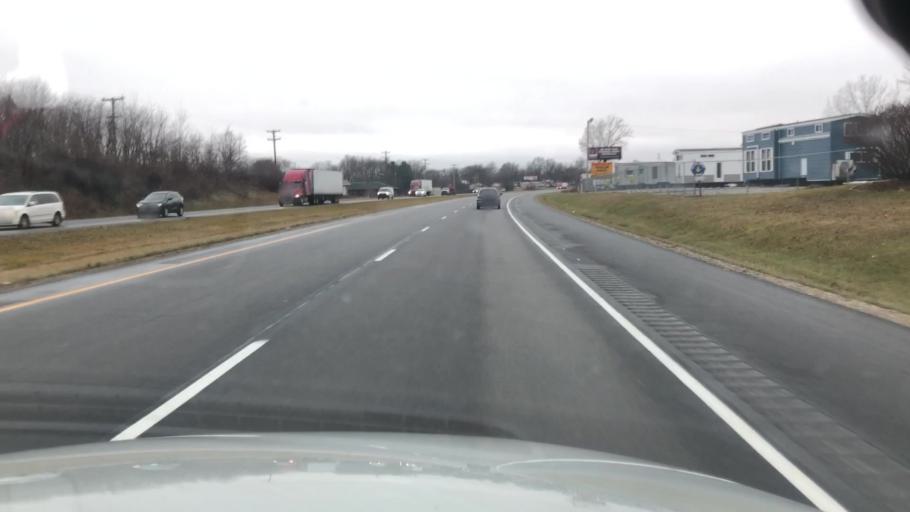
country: US
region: Indiana
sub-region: Kosciusko County
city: Pierceton
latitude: 41.1984
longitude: -85.6929
